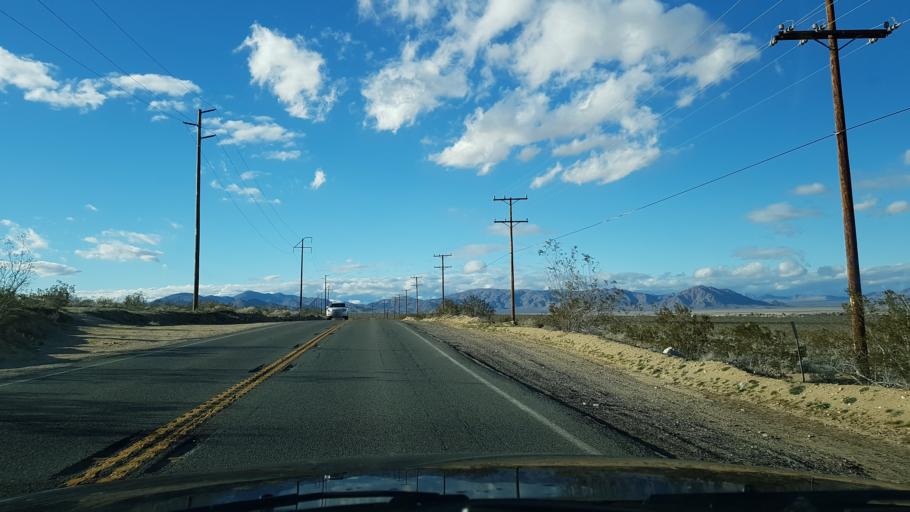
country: US
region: California
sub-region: San Bernardino County
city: Lucerne Valley
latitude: 34.4177
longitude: -116.9117
